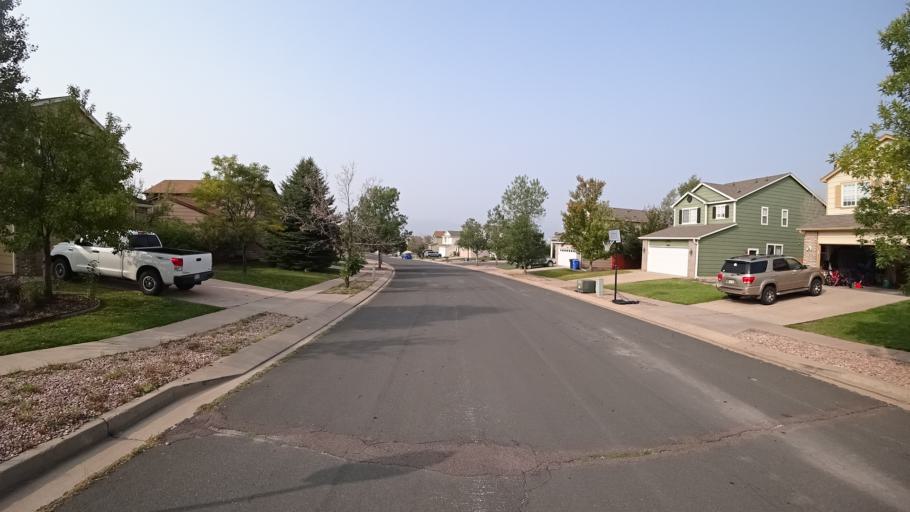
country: US
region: Colorado
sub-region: El Paso County
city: Cimarron Hills
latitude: 38.9354
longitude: -104.7280
